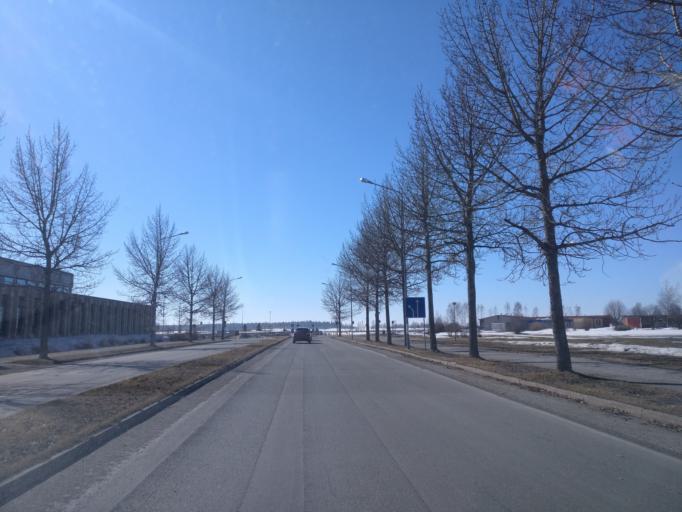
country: FI
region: Lapland
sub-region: Kemi-Tornio
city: Kemi
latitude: 65.7374
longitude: 24.5557
